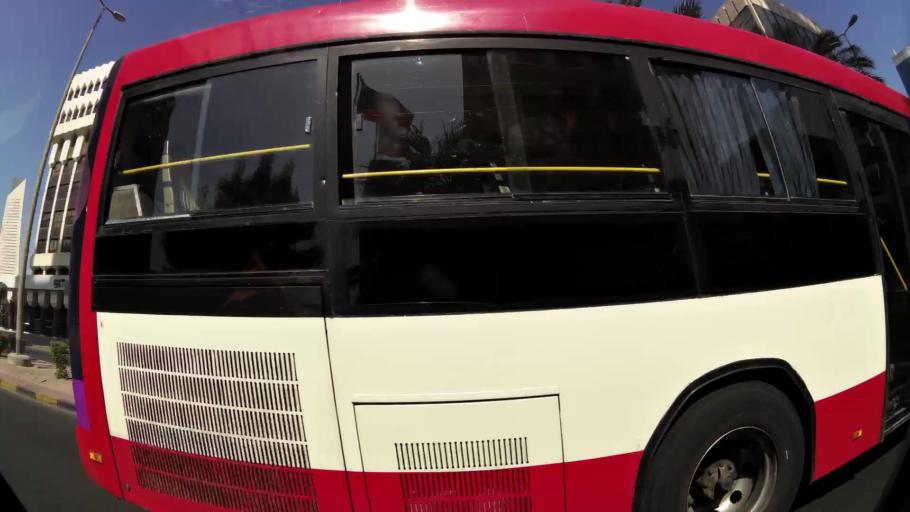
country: KW
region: Al Asimah
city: Kuwait City
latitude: 29.3814
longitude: 47.9852
